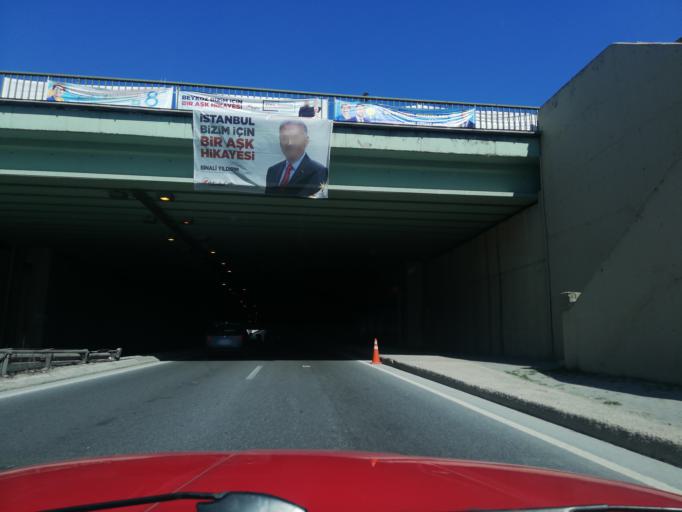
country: TR
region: Istanbul
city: Umraniye
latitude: 41.0940
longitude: 29.0961
